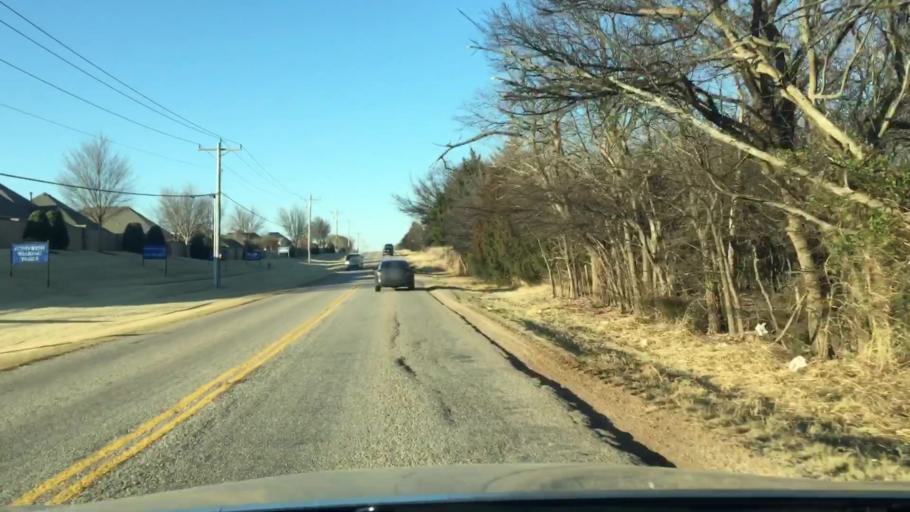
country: US
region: Oklahoma
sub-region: Oklahoma County
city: The Village
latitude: 35.6263
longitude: -97.6208
